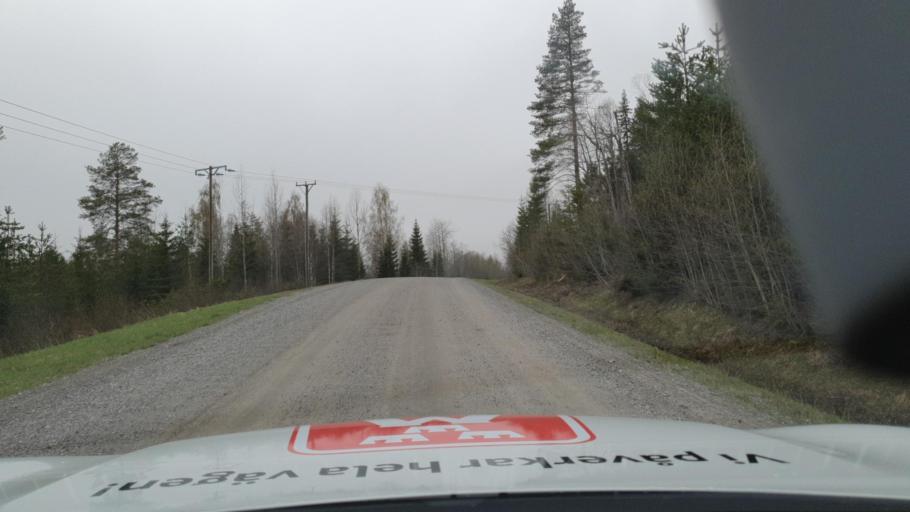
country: SE
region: Vaesterbotten
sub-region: Nordmalings Kommun
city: Nordmaling
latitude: 63.7651
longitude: 19.4459
